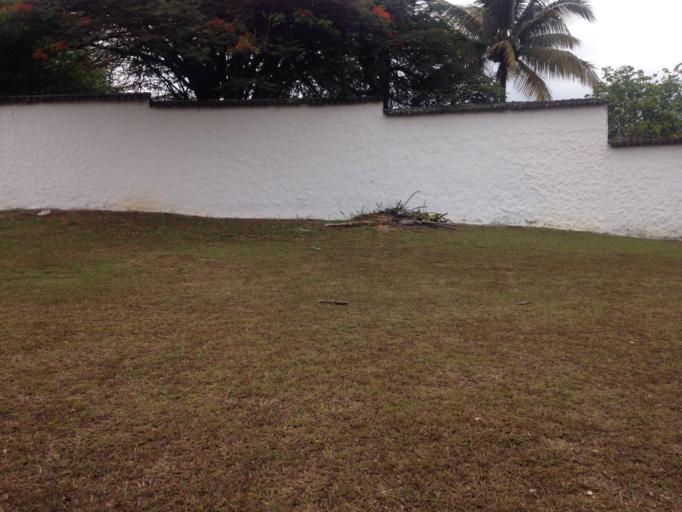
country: CO
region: Valle del Cauca
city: Cali
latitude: 3.3622
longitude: -76.5359
